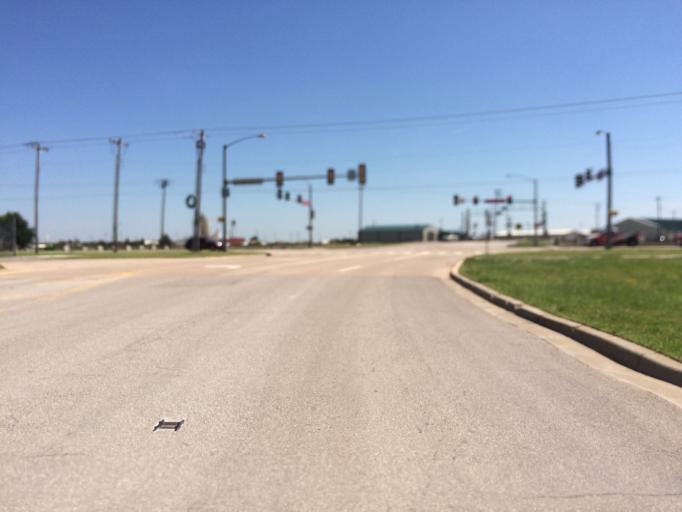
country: US
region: Oklahoma
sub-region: Cleveland County
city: Norman
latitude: 35.2466
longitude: -97.4615
